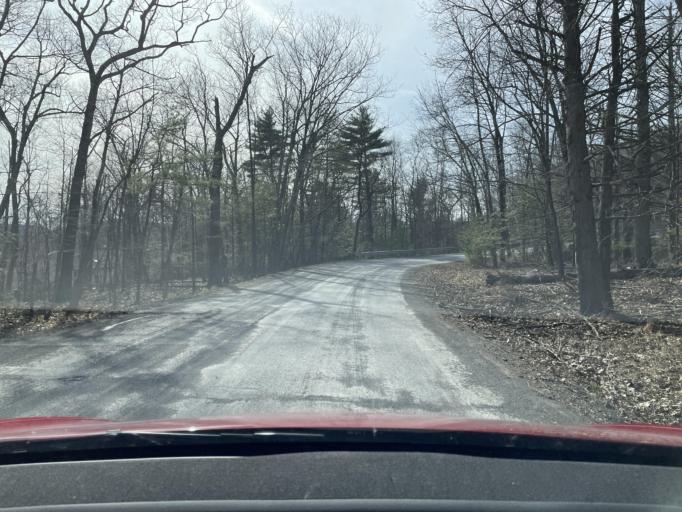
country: US
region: New York
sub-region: Ulster County
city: Woodstock
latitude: 42.0595
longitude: -74.1111
